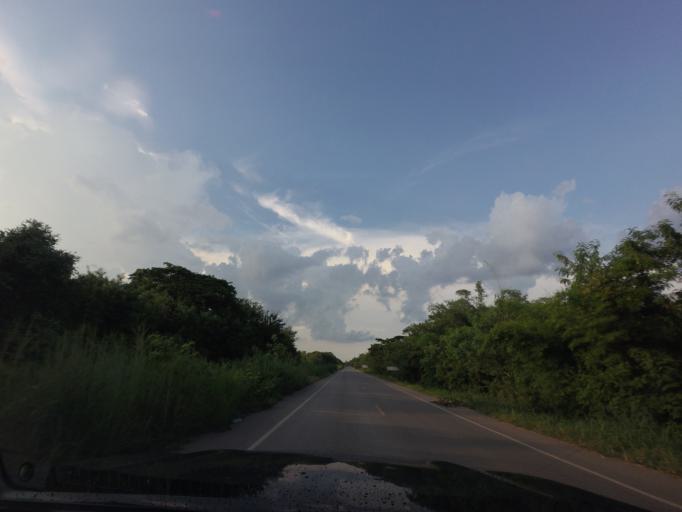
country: TH
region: Khon Kaen
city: Khon Kaen
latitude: 16.4057
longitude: 102.8642
